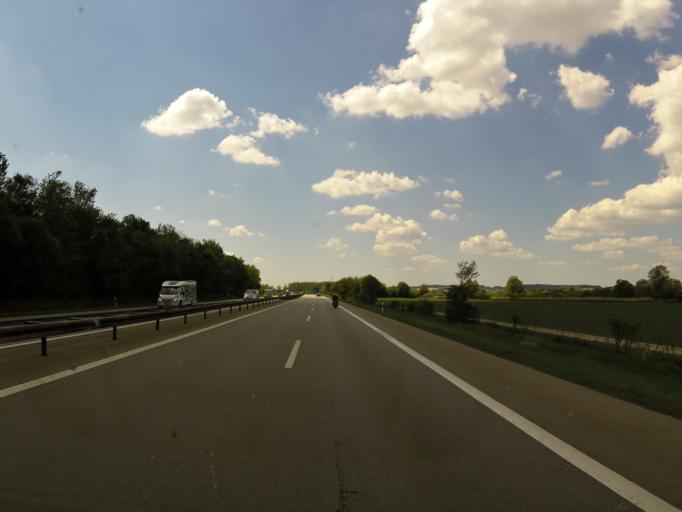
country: DE
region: Bavaria
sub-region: Lower Bavaria
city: Pilsting
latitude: 48.6846
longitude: 12.6276
